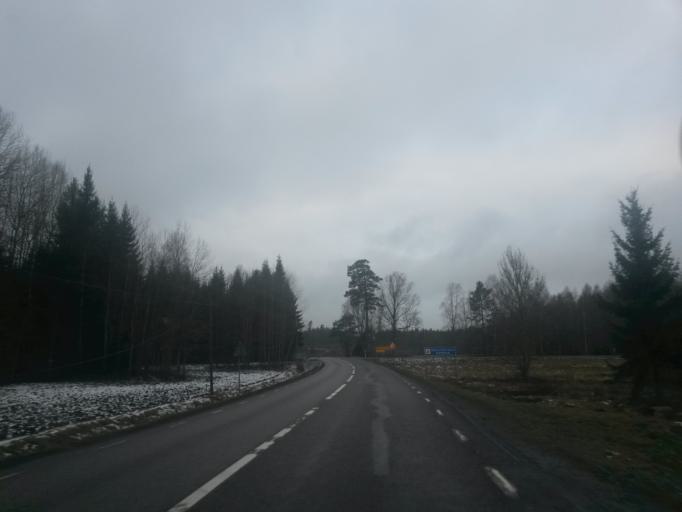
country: SE
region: Vaestra Goetaland
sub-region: Alingsas Kommun
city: Sollebrunn
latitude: 58.1328
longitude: 12.4843
